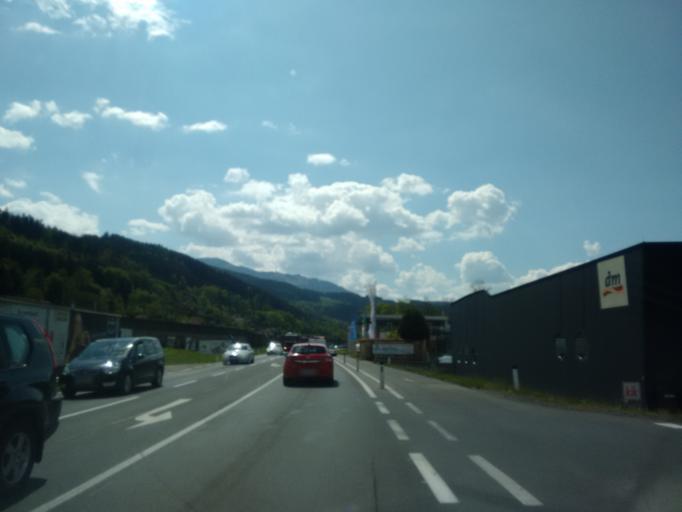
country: AT
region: Styria
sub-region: Politischer Bezirk Bruck-Muerzzuschlag
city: Bruck an der Mur
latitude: 47.4037
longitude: 15.2521
